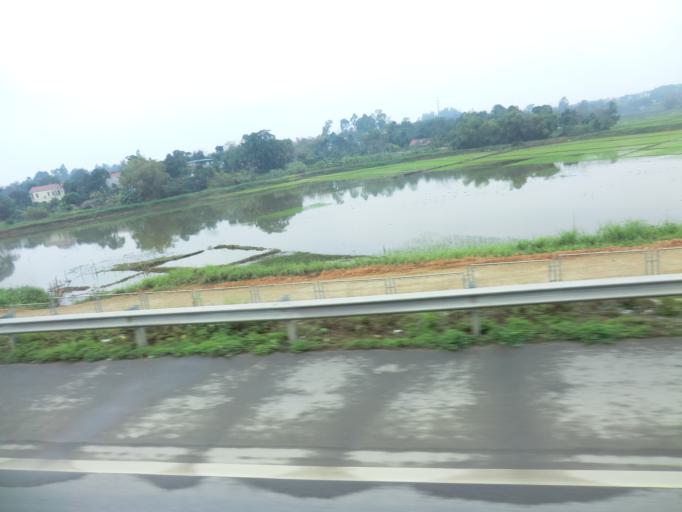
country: VN
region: Phu Tho
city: Phong Chau
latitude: 21.3908
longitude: 105.3430
